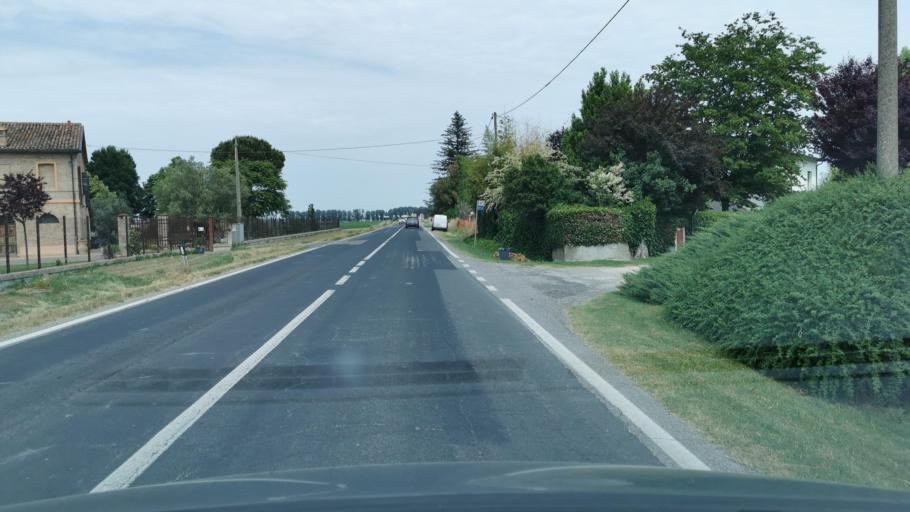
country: IT
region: Emilia-Romagna
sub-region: Provincia di Ravenna
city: Glorie
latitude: 44.4938
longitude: 12.0766
